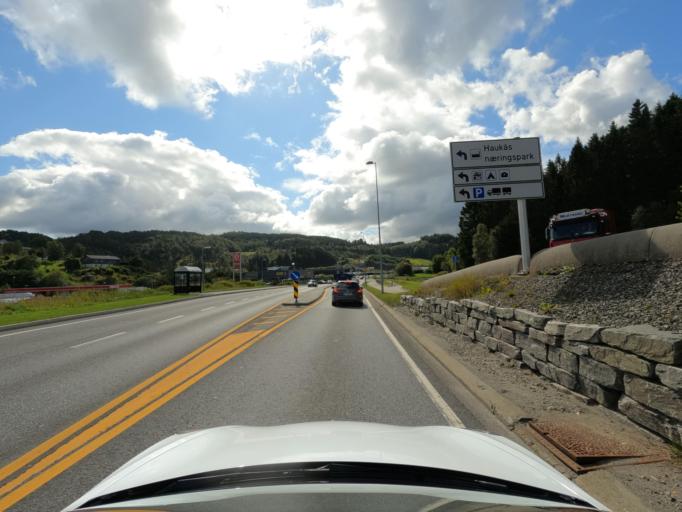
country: NO
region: Hordaland
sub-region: Bergen
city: Hylkje
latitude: 60.4854
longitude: 5.3759
